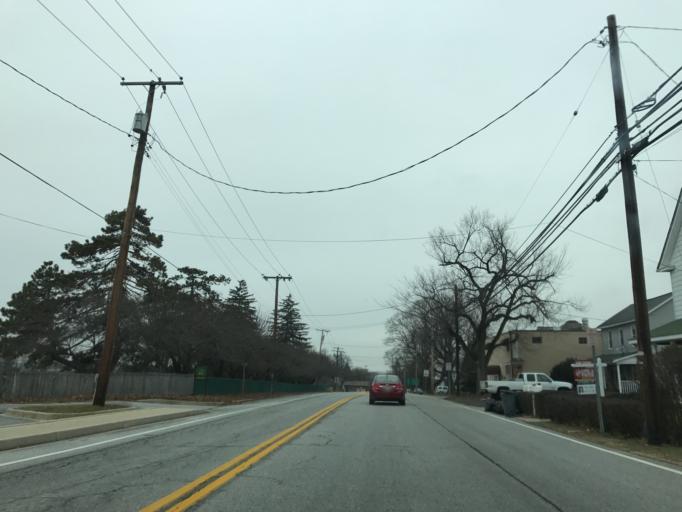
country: US
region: Maryland
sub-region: Carroll County
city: Westminster
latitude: 39.5881
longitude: -76.9991
